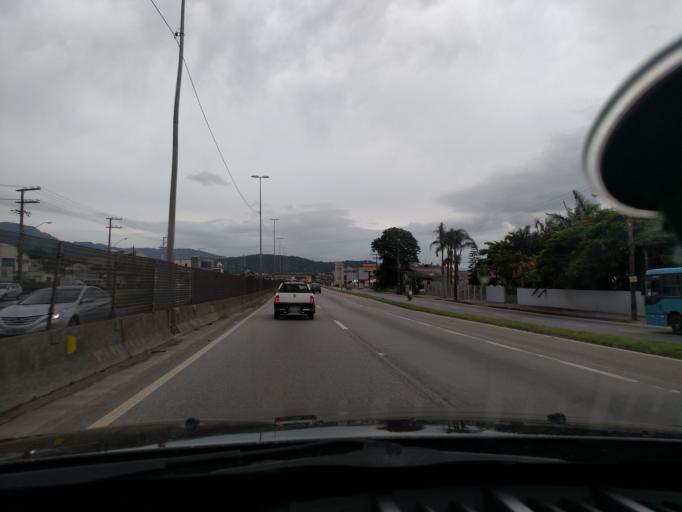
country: BR
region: Santa Catarina
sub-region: Biguacu
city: Biguacu
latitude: -27.5362
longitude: -48.6274
